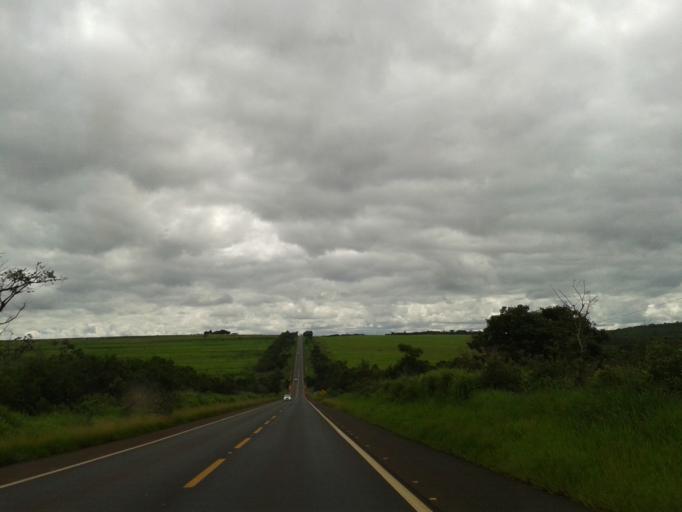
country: BR
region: Minas Gerais
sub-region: Monte Alegre De Minas
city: Monte Alegre de Minas
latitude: -18.8802
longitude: -49.1582
